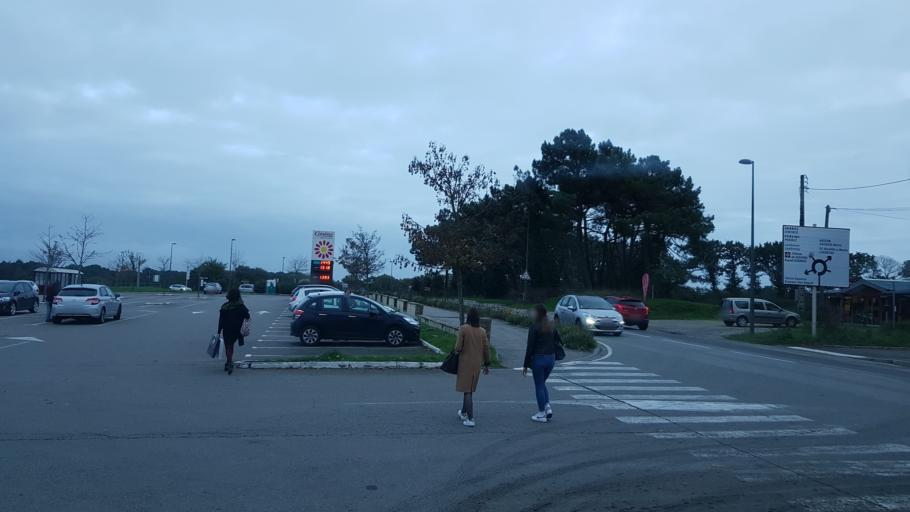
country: FR
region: Brittany
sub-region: Departement du Morbihan
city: Sarzeau
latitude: 47.5276
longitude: -2.7567
